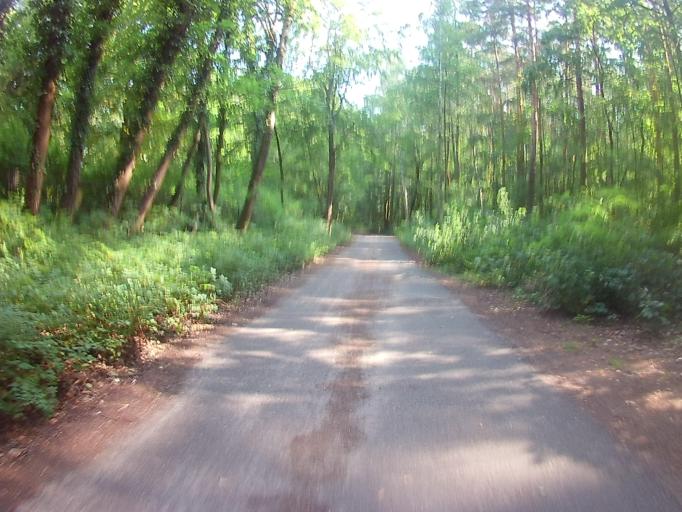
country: DE
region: Berlin
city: Grunau
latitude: 52.4081
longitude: 13.5922
